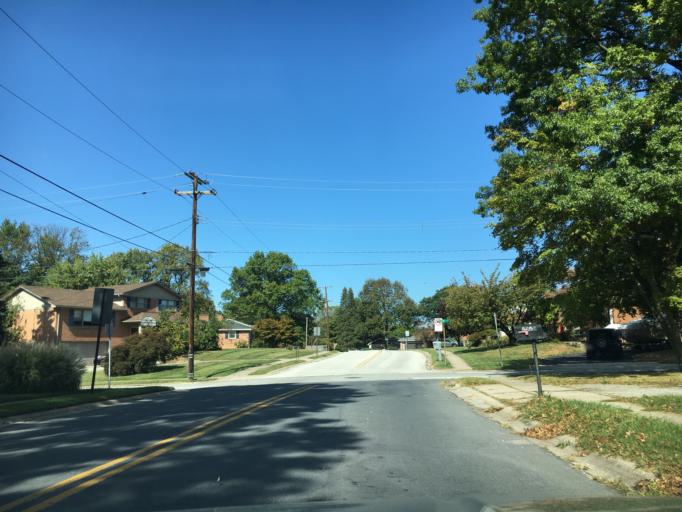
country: US
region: Pennsylvania
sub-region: York County
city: East York
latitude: 39.9645
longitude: -76.6737
